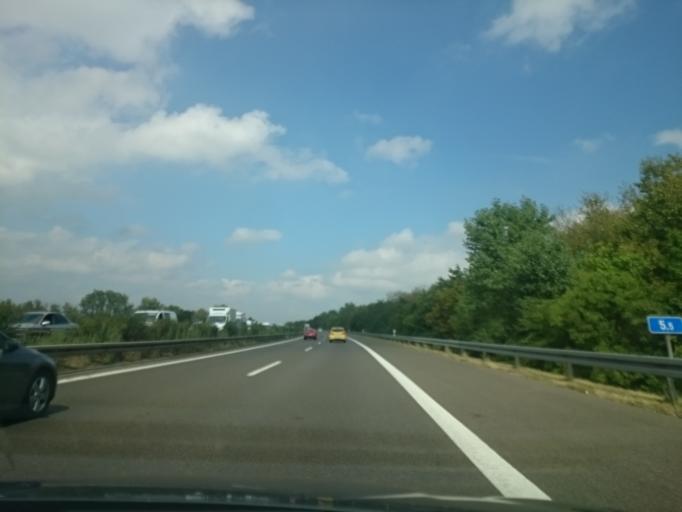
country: DE
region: Brandenburg
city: Bernau bei Berlin
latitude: 52.6635
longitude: 13.5698
